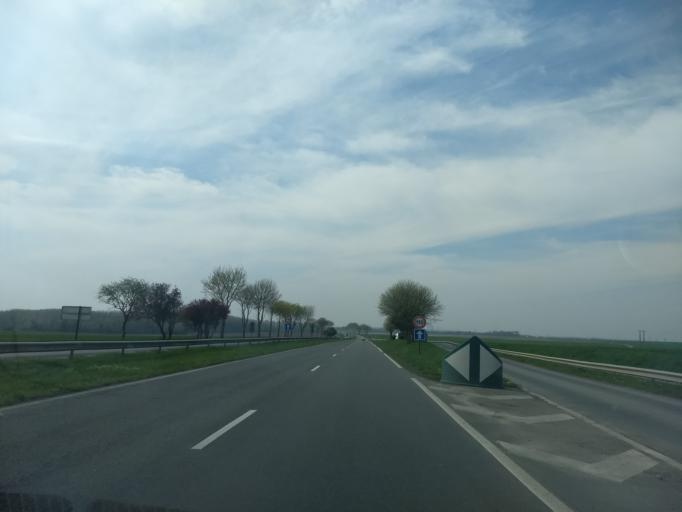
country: FR
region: Nord-Pas-de-Calais
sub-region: Departement du Pas-de-Calais
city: Vitry-en-Artois
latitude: 50.3330
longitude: 2.9700
